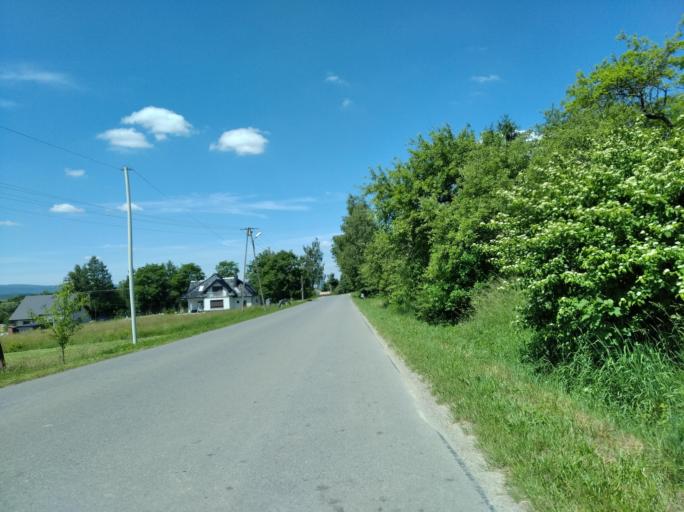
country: PL
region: Subcarpathian Voivodeship
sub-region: Powiat jasielski
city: Nowy Zmigrod
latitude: 49.6181
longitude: 21.5654
